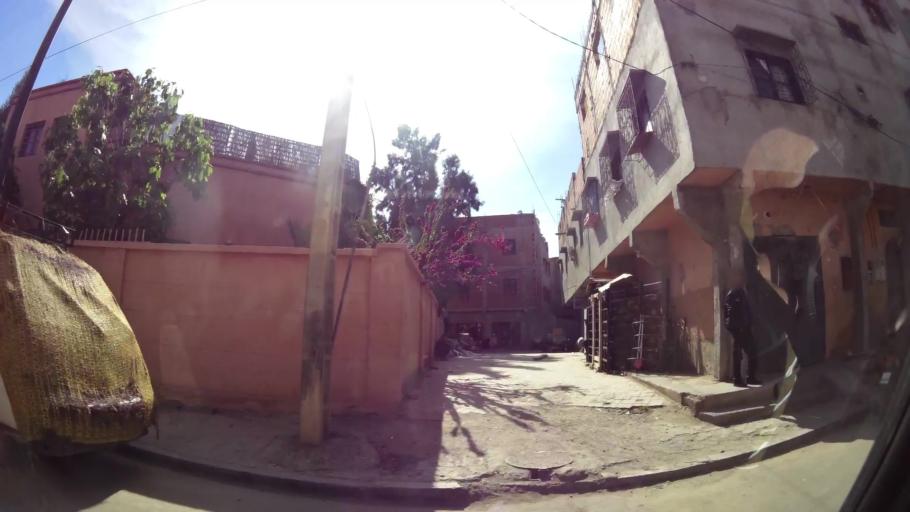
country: MA
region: Marrakech-Tensift-Al Haouz
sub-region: Marrakech
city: Marrakesh
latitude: 31.6360
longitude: -7.9769
